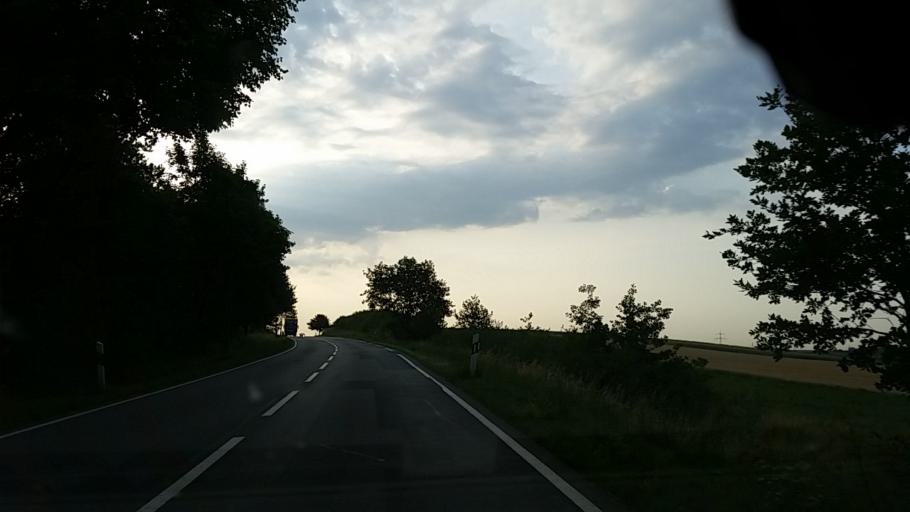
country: DE
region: Lower Saxony
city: Rennau
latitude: 52.2992
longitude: 10.8825
